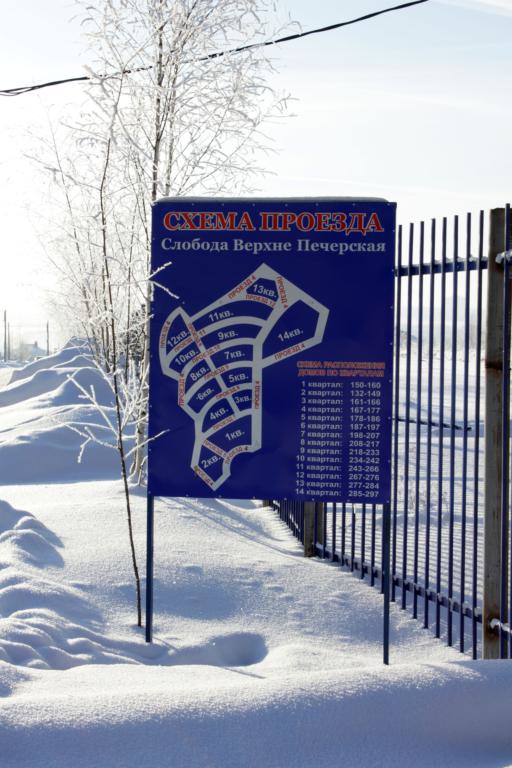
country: RU
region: Nizjnij Novgorod
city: Afonino
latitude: 56.2837
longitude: 44.0663
